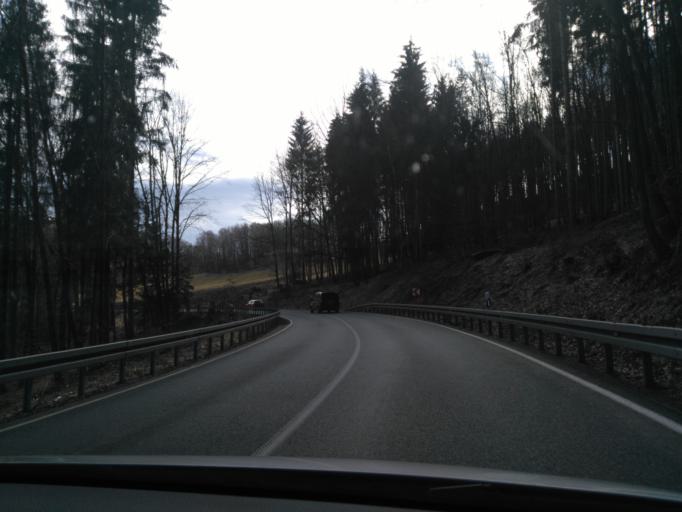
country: DE
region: Saxony
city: Wolkenstein
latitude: 50.6592
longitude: 13.0565
